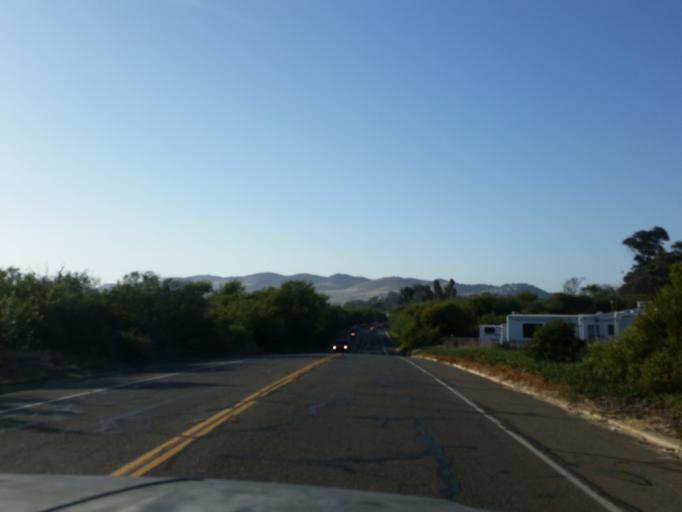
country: US
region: California
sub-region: San Luis Obispo County
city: Grover Beach
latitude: 35.1185
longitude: -120.6285
